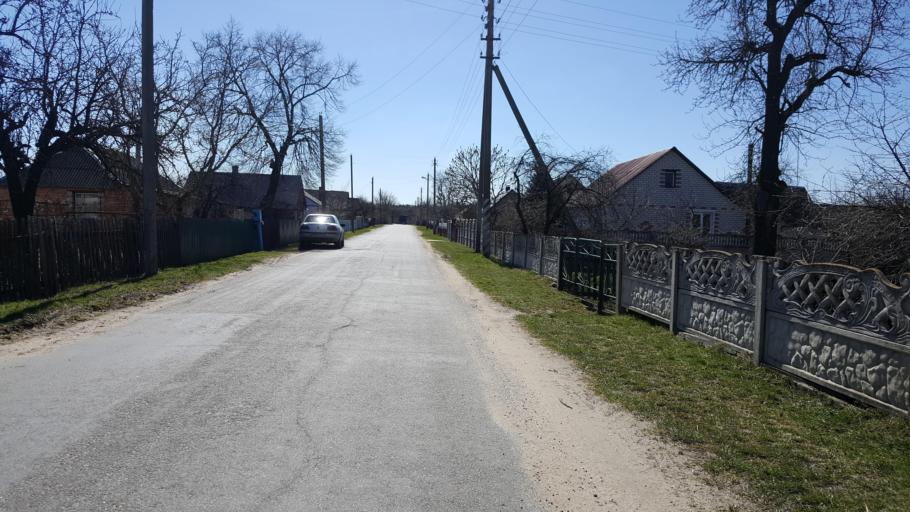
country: BY
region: Brest
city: Kamyanyets
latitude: 52.2885
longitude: 23.8598
